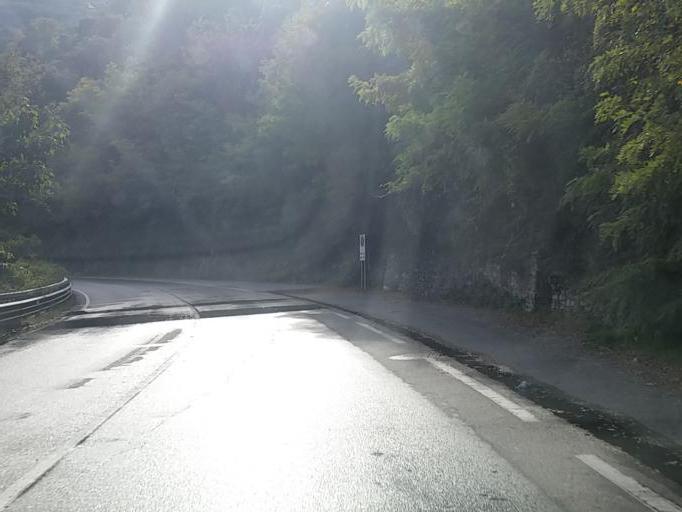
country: IT
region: Piedmont
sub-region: Provincia Verbano-Cusio-Ossola
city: Cannobio
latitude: 46.0500
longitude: 8.7053
